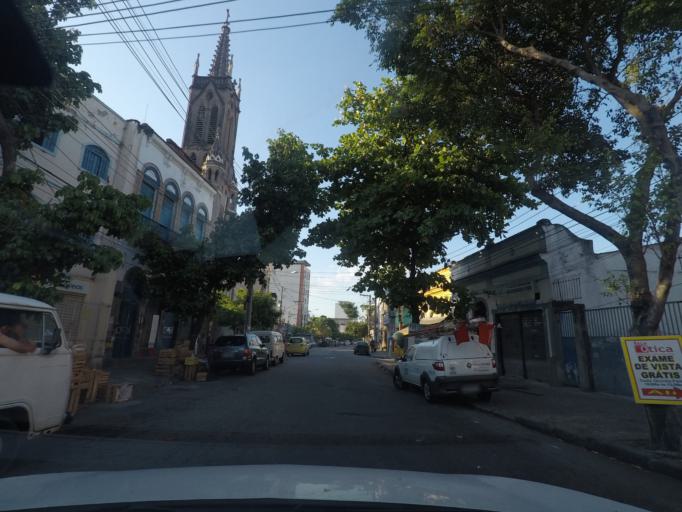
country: BR
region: Rio de Janeiro
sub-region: Rio De Janeiro
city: Rio de Janeiro
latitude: -22.9165
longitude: -43.1953
